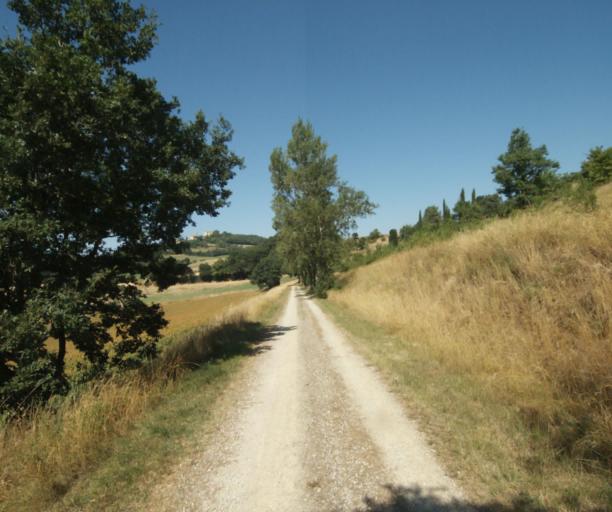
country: FR
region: Midi-Pyrenees
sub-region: Departement de la Haute-Garonne
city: Revel
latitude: 43.5120
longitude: 1.9449
